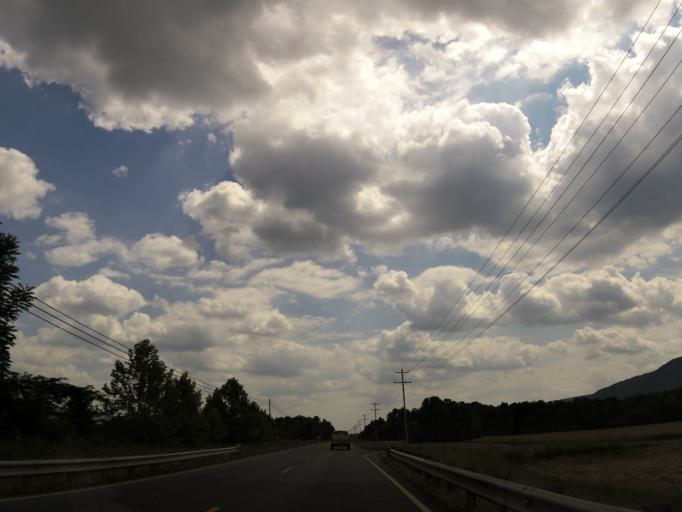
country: US
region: Tennessee
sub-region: Sequatchie County
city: Dunlap
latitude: 35.4121
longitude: -85.3651
